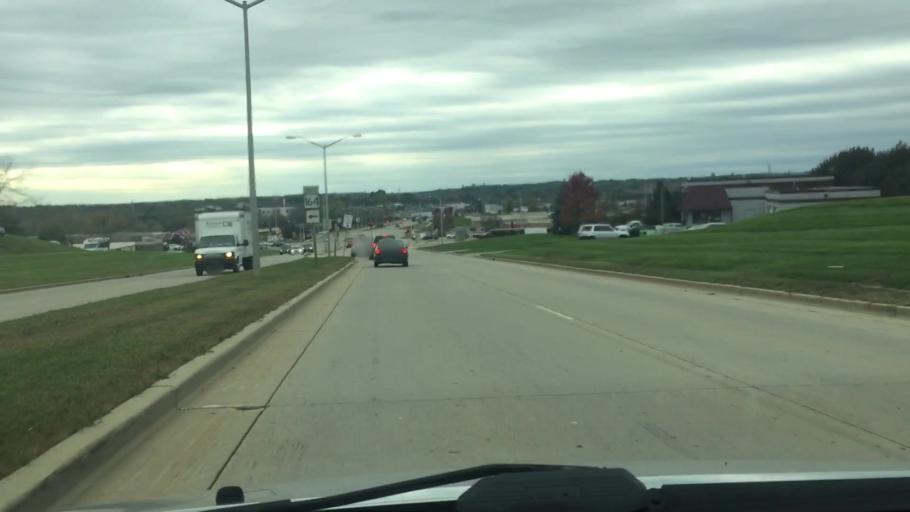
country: US
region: Wisconsin
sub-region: Waukesha County
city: Waukesha
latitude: 43.0219
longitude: -88.1982
